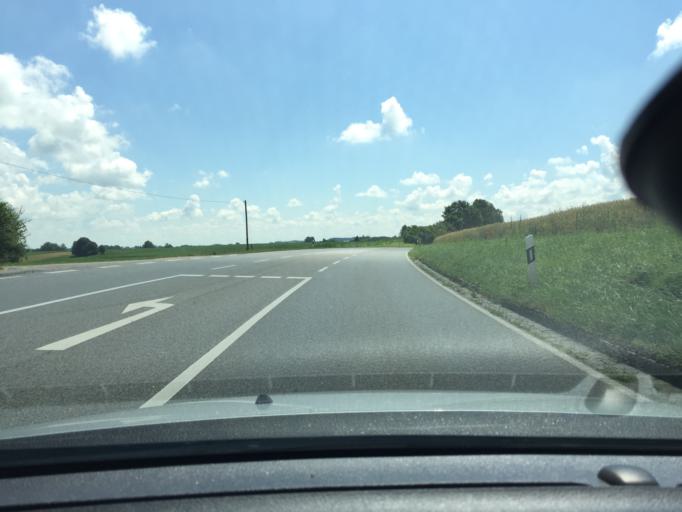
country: DE
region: Bavaria
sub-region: Upper Bavaria
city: Dorfen
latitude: 48.2877
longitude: 12.1295
